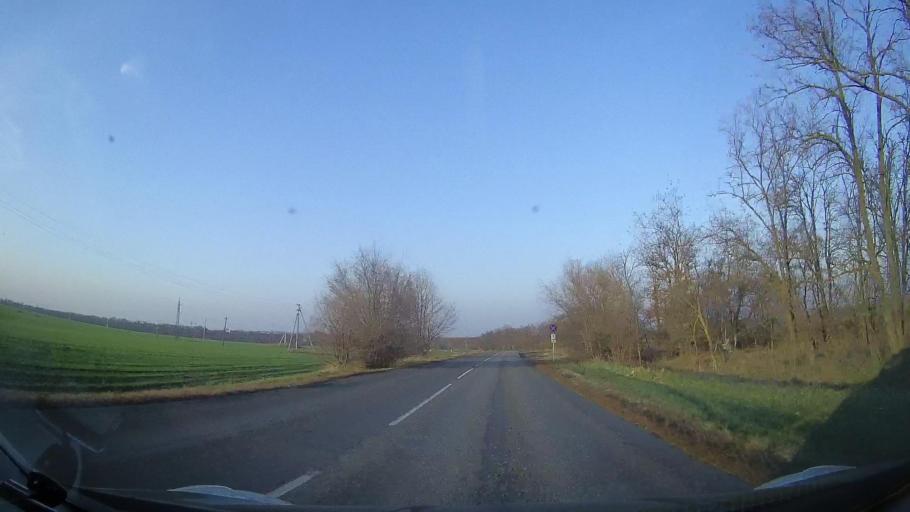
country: RU
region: Rostov
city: Ol'ginskaya
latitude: 47.1059
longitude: 39.9776
